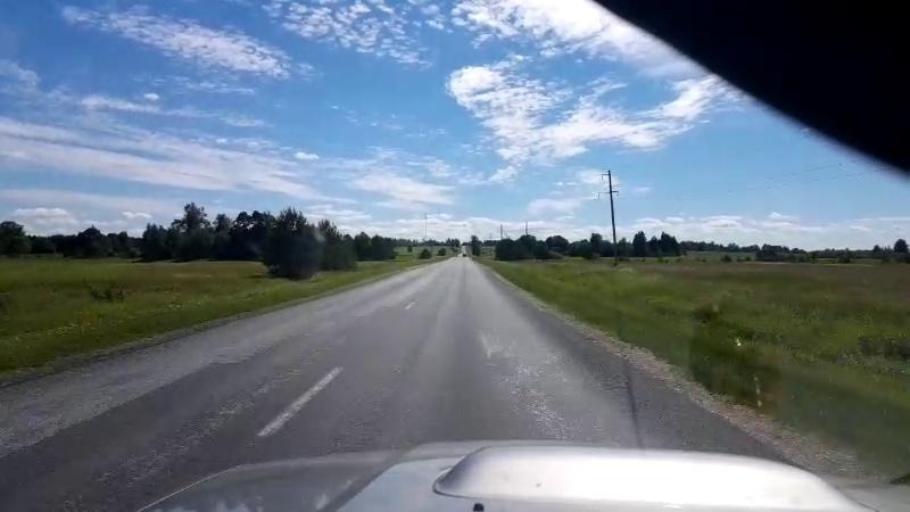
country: EE
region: Laeaene-Virumaa
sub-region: Rakke vald
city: Rakke
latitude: 58.8639
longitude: 26.2939
